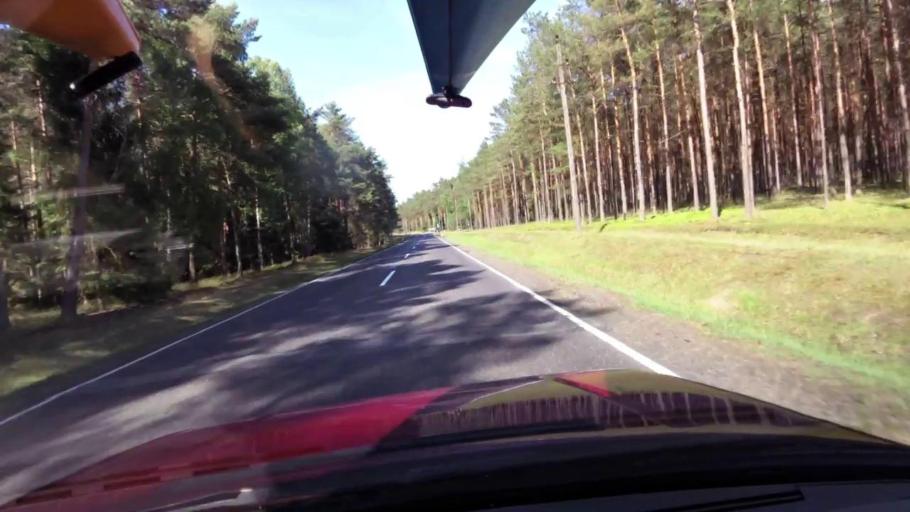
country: PL
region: Pomeranian Voivodeship
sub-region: Powiat bytowski
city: Trzebielino
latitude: 54.1645
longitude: 17.0573
